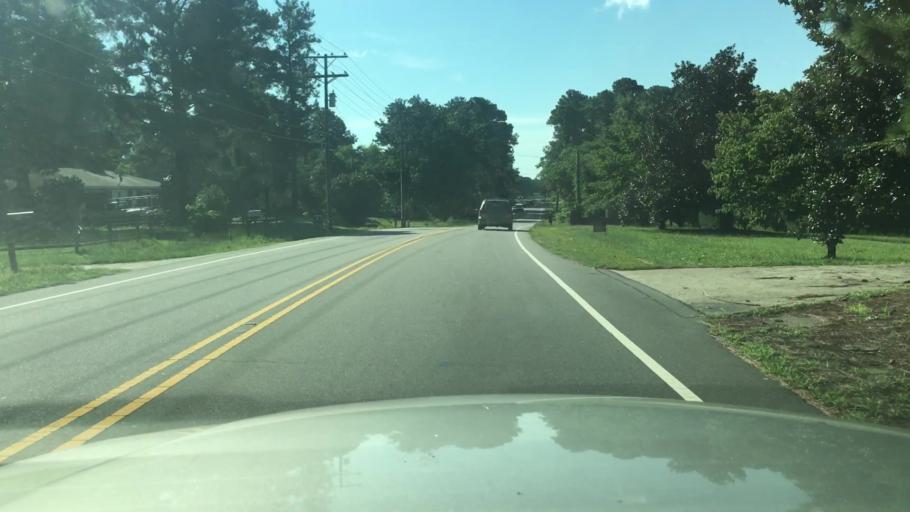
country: US
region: North Carolina
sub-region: Cumberland County
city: Fayetteville
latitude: 35.1158
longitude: -78.9091
